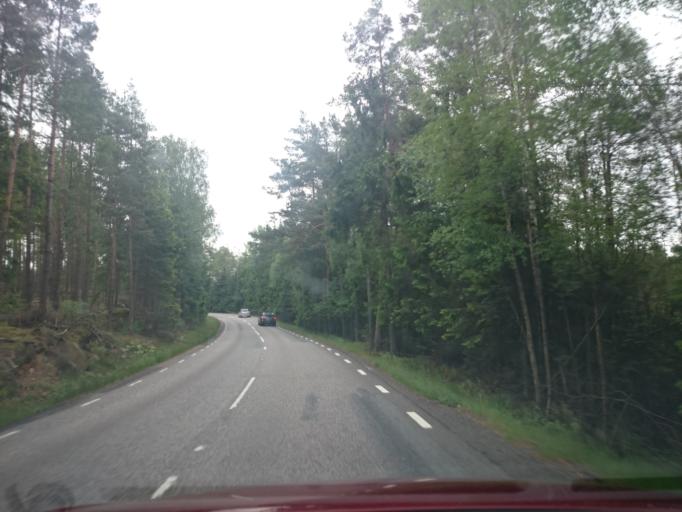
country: SE
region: Vaestra Goetaland
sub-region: Lerums Kommun
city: Stenkullen
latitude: 57.7167
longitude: 12.3450
